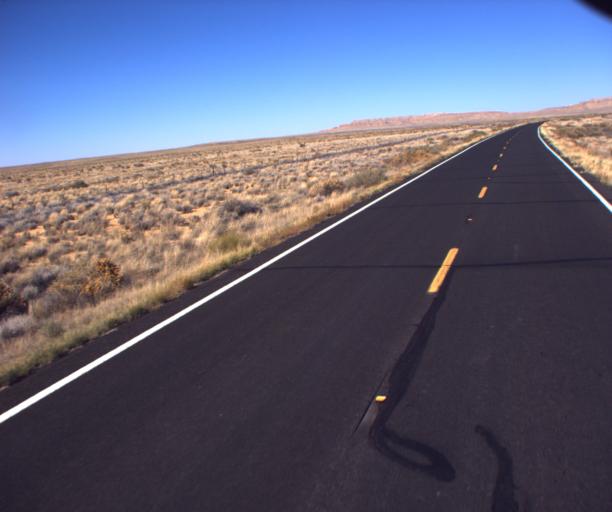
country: US
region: Arizona
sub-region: Navajo County
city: First Mesa
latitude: 35.7272
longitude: -110.5173
